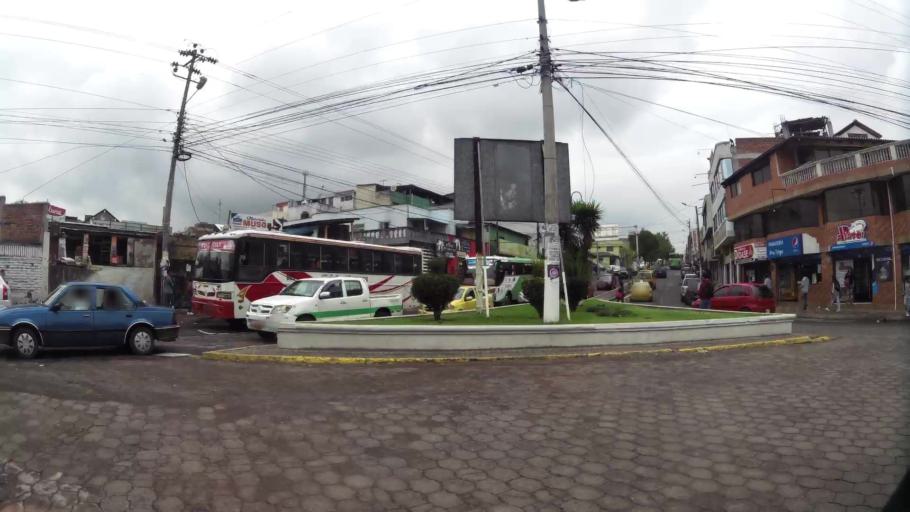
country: EC
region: Pichincha
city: Sangolqui
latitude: -0.3341
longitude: -78.4406
